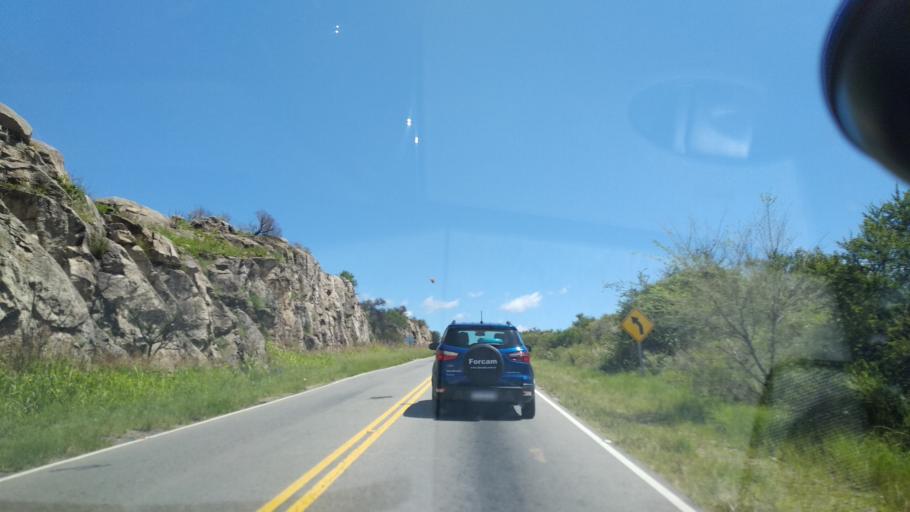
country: AR
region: Cordoba
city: Villa Cura Brochero
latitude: -31.6967
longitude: -65.0597
